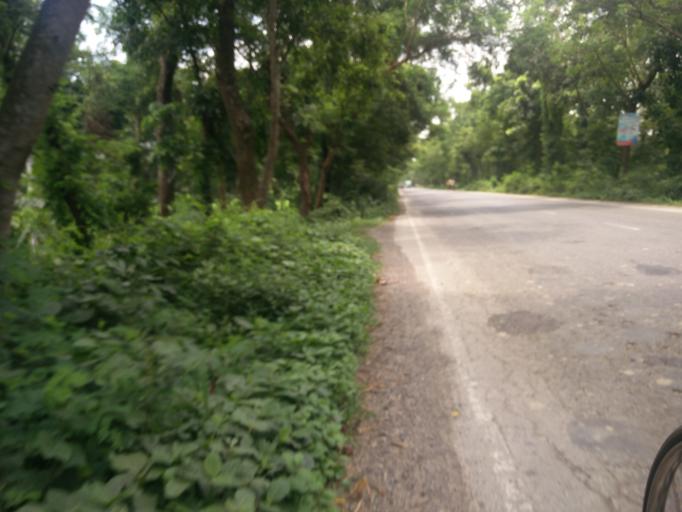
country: BD
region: Khulna
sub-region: Magura
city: Magura
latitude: 23.5464
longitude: 89.5228
